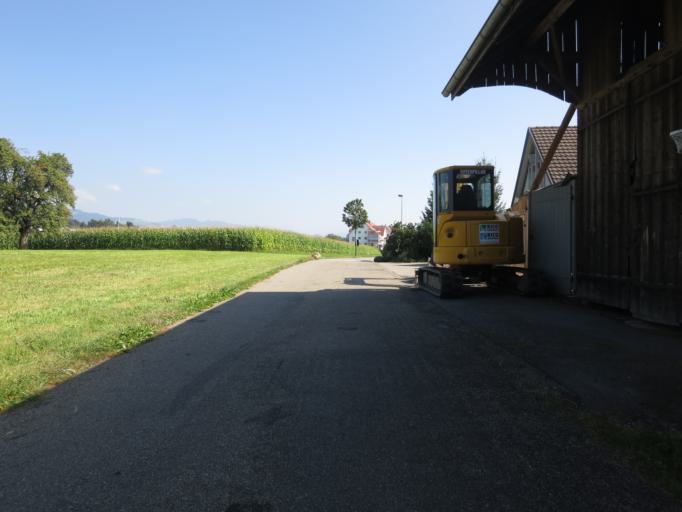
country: CH
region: Zurich
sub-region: Bezirk Hinwil
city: Wolfhausen
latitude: 47.2558
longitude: 8.7898
